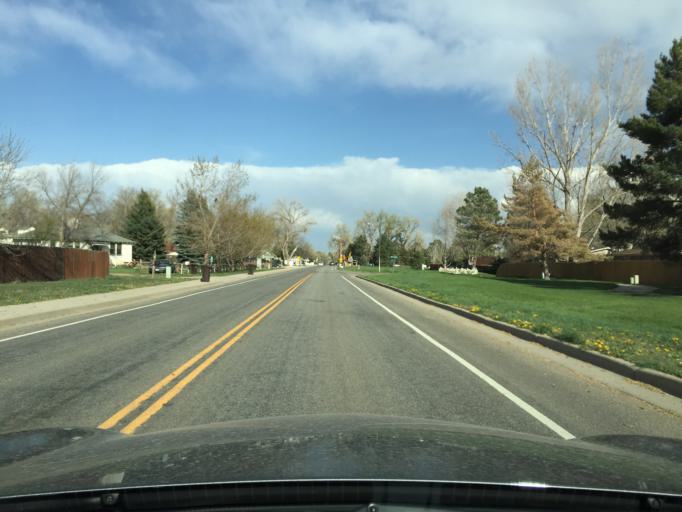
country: US
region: Colorado
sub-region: Boulder County
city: Niwot
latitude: 40.1017
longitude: -105.1726
